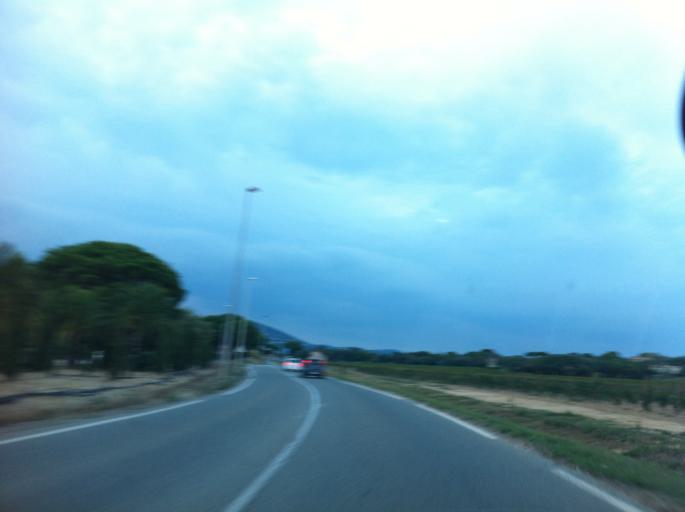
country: FR
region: Provence-Alpes-Cote d'Azur
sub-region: Departement du Var
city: Gassin
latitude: 43.2557
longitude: 6.5945
